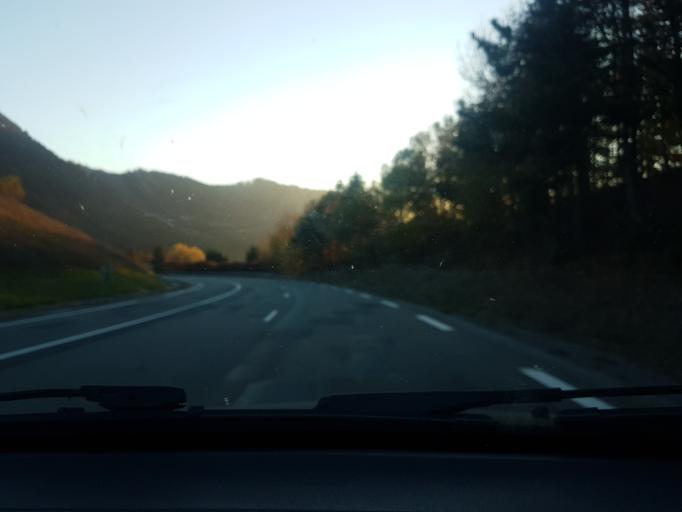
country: FR
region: Franche-Comte
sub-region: Departement du Doubs
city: Villers-le-Lac
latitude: 47.0589
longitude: 6.6772
